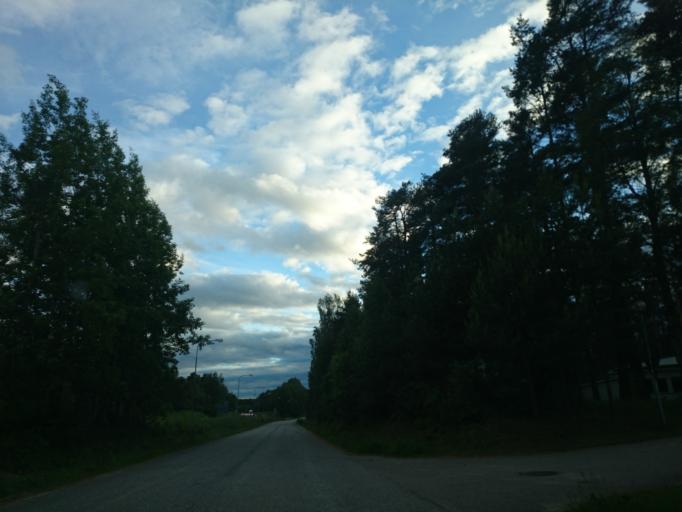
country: SE
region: Vaesternorrland
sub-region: Timra Kommun
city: Bergeforsen
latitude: 62.5145
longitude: 17.3763
